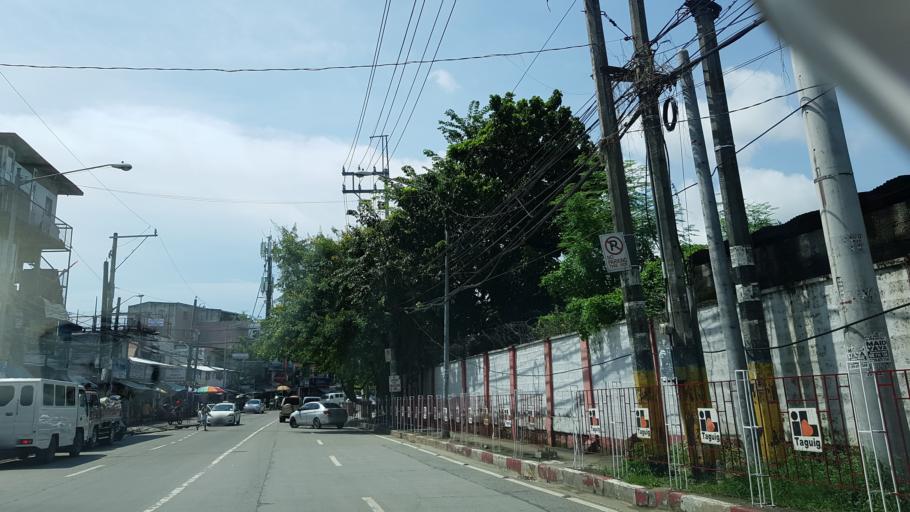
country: PH
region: Metro Manila
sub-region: Makati City
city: Makati City
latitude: 14.5260
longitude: 121.0271
